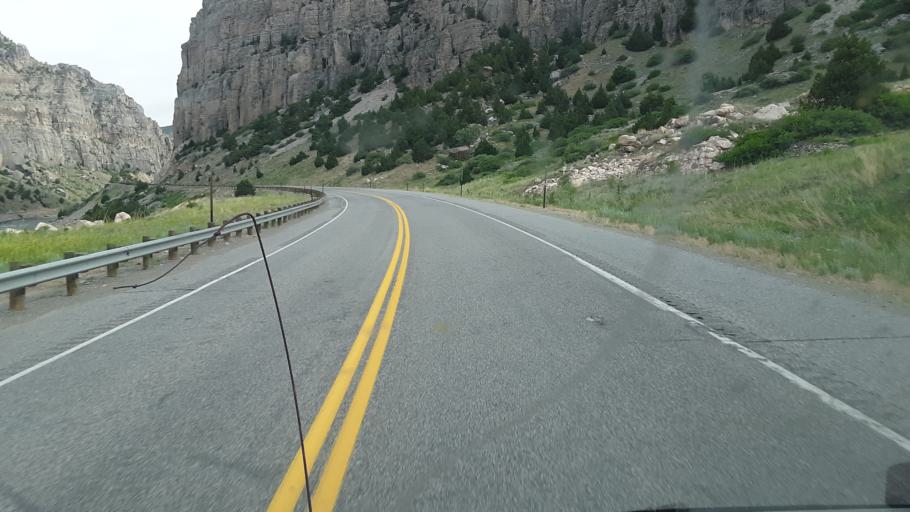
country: US
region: Wyoming
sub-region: Hot Springs County
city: Thermopolis
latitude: 43.5261
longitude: -108.1750
